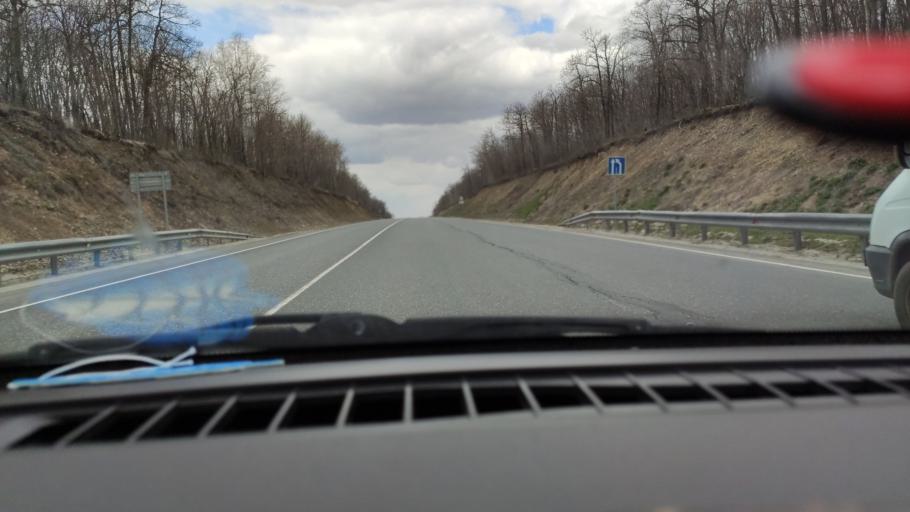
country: RU
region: Saratov
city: Vol'sk
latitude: 52.1082
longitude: 47.3946
